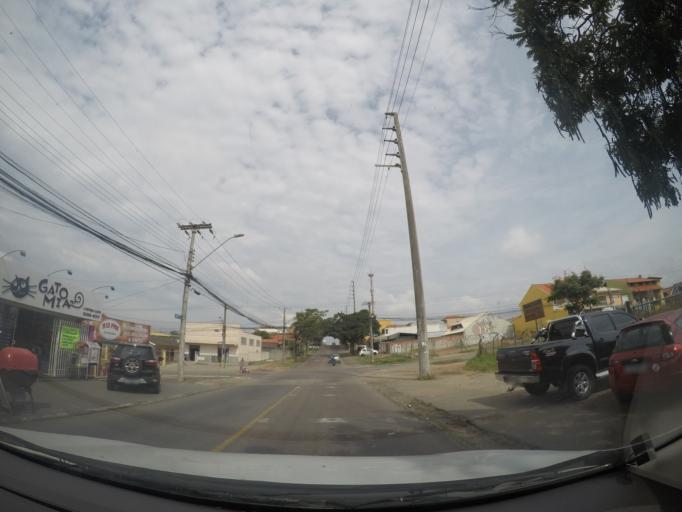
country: BR
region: Parana
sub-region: Sao Jose Dos Pinhais
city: Sao Jose dos Pinhais
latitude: -25.5181
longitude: -49.2770
